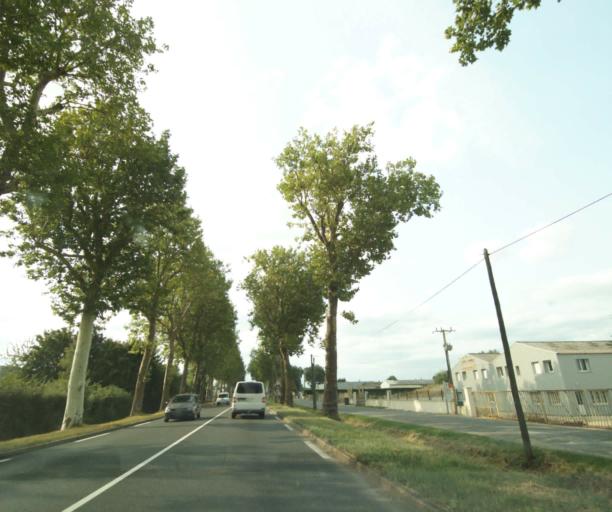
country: FR
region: Centre
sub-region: Departement d'Indre-et-Loire
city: Cormery
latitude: 47.2606
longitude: 0.8381
